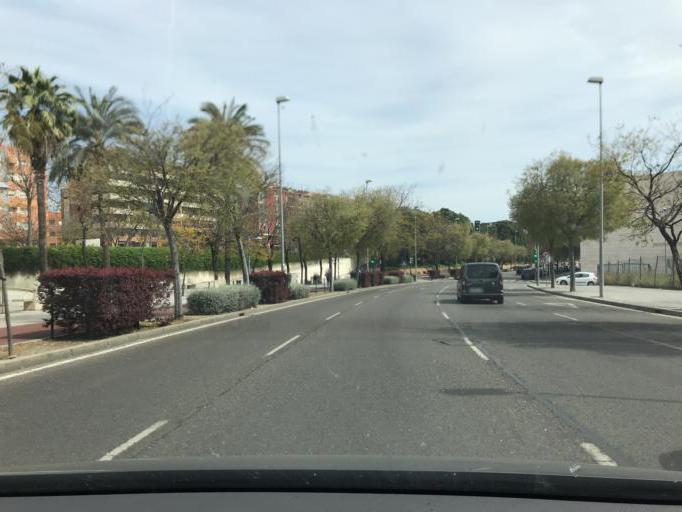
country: ES
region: Andalusia
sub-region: Province of Cordoba
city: Cordoba
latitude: 37.8923
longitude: -4.7801
